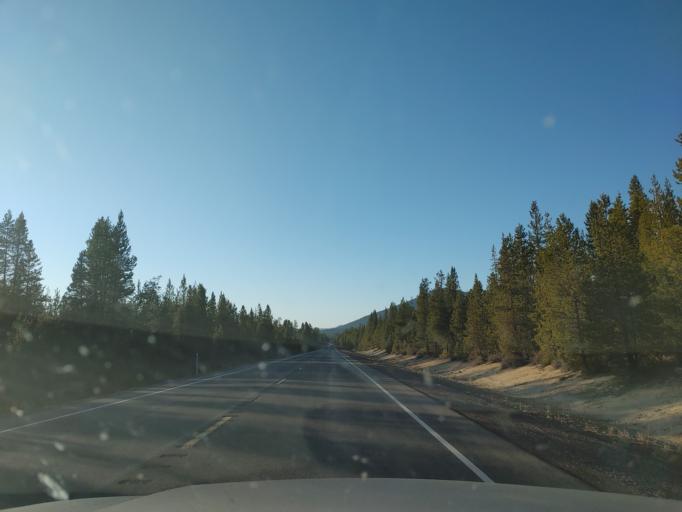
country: US
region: Oregon
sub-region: Deschutes County
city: La Pine
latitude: 43.4014
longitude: -121.8220
